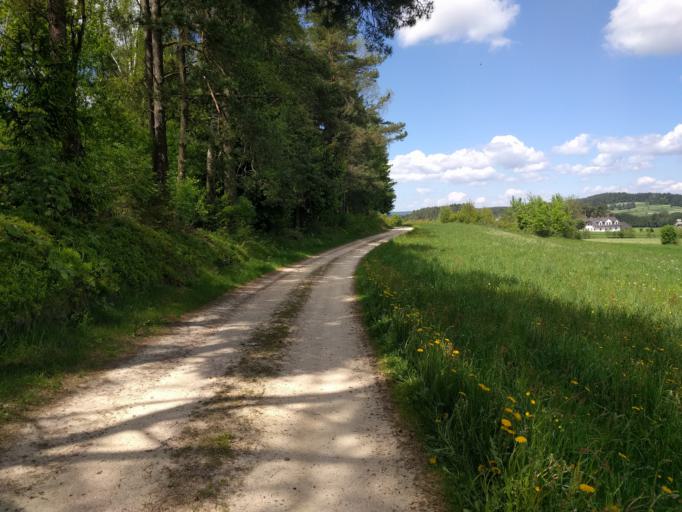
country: AT
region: Lower Austria
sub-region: Politischer Bezirk Zwettl
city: Langschlag
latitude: 48.5840
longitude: 14.8955
